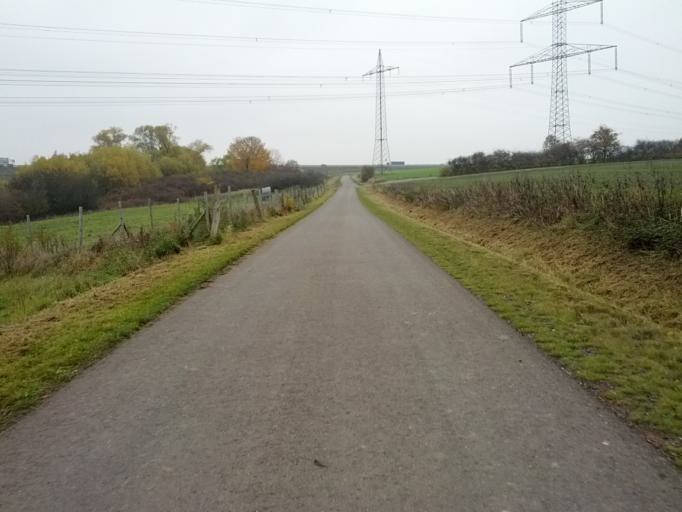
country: DE
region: Thuringia
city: Haina
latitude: 50.9887
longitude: 10.4473
